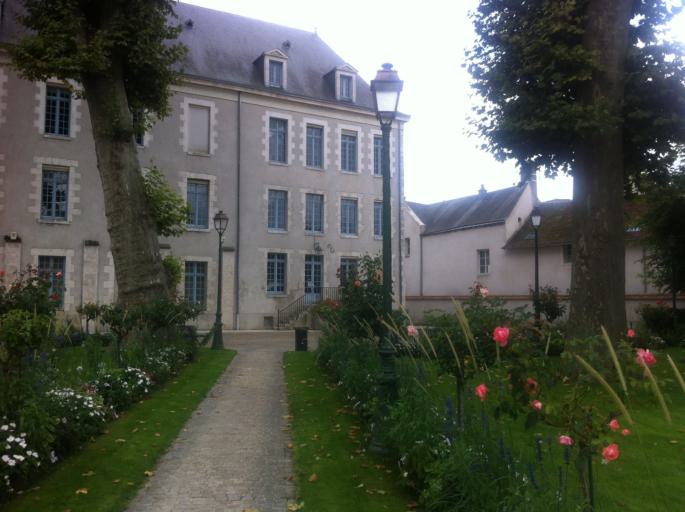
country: FR
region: Centre
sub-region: Departement du Loiret
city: Chalette-sur-Loing
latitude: 47.9981
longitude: 2.7307
